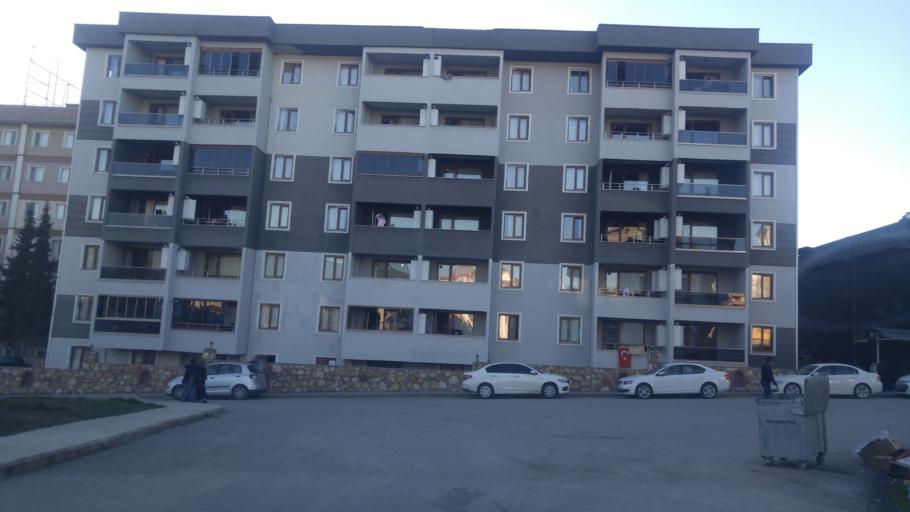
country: TR
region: Karabuk
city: Karabuk
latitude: 41.2156
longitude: 32.6622
